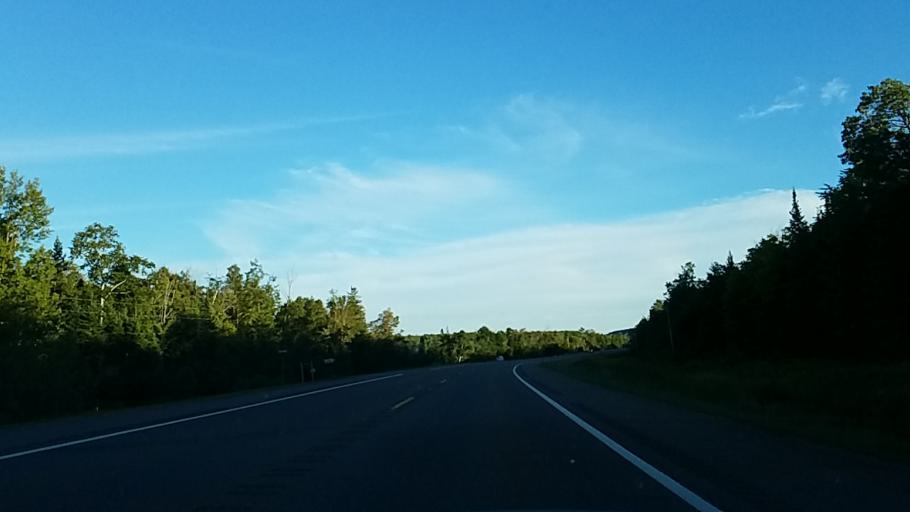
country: US
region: Michigan
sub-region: Alger County
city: Munising
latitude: 46.4567
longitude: -86.8911
